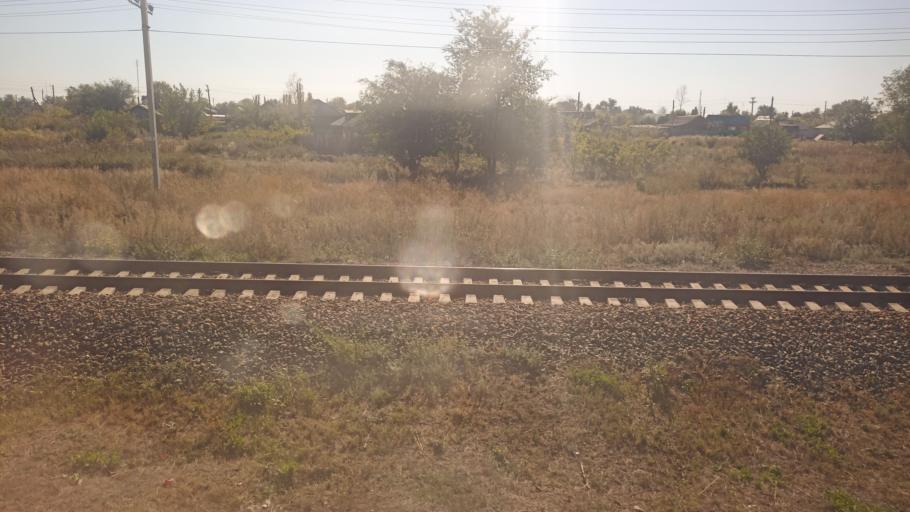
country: RU
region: Saratov
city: Pushkino
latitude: 51.2342
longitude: 46.9837
